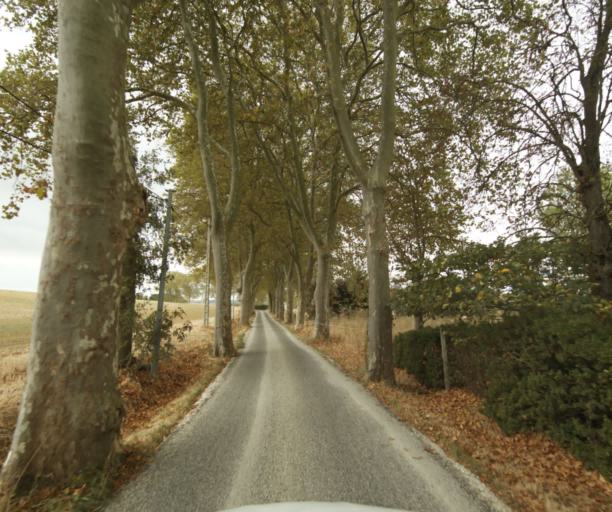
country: FR
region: Midi-Pyrenees
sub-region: Departement de la Haute-Garonne
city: Villefranche-de-Lauragais
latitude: 43.4015
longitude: 1.7330
